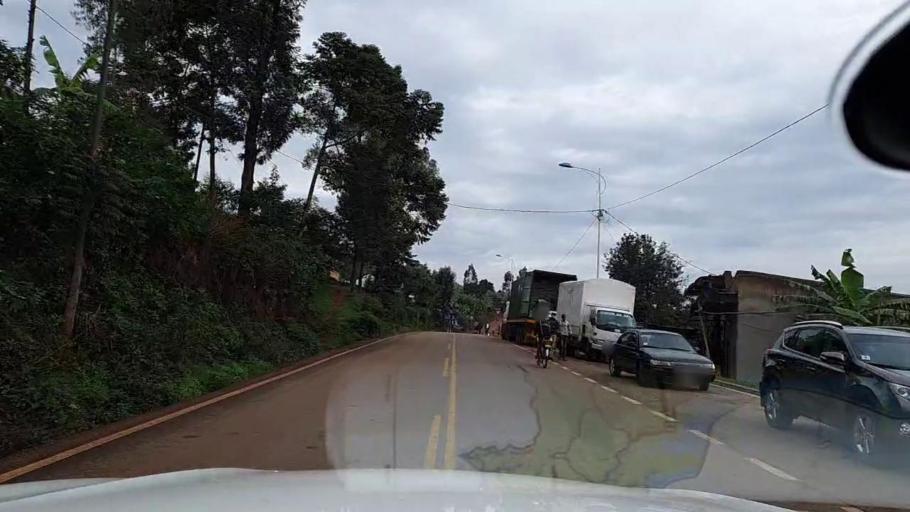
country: RW
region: Southern Province
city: Butare
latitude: -2.5800
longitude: 29.7348
